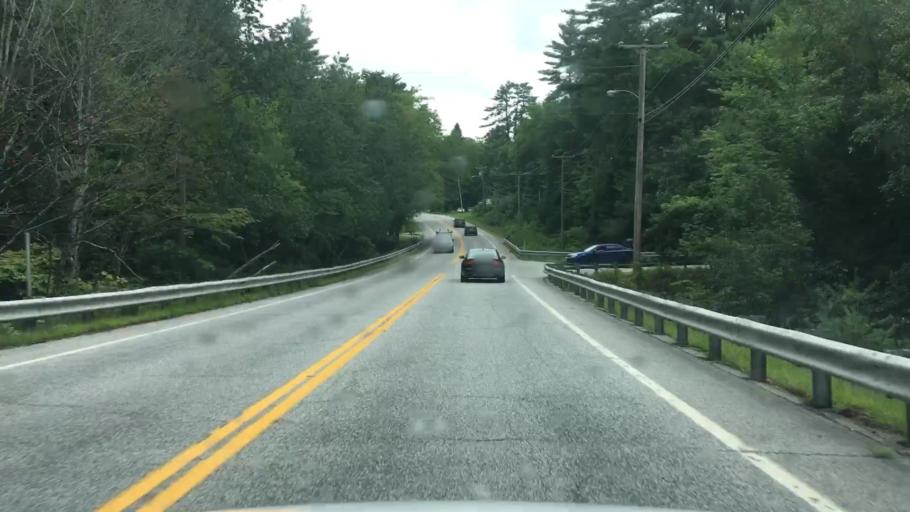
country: US
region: Maine
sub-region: York County
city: Cornish
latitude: 43.8266
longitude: -70.7754
